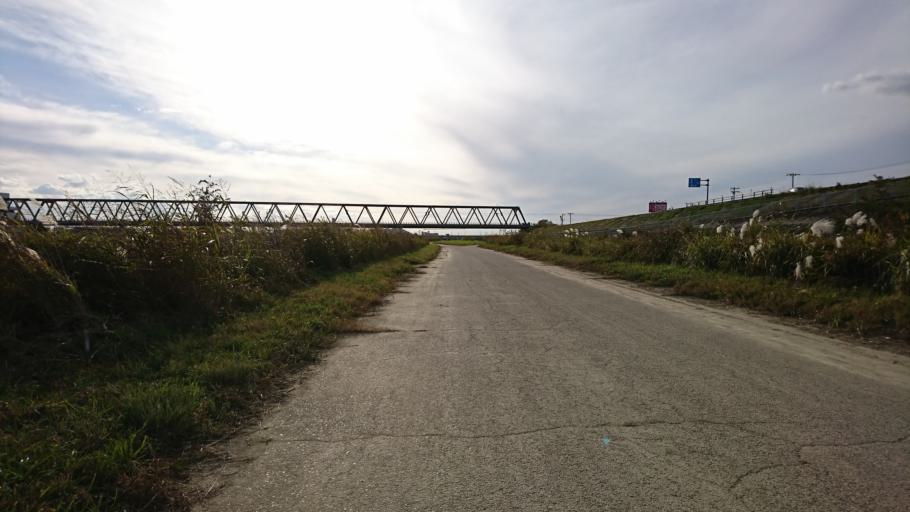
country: JP
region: Hyogo
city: Kakogawacho-honmachi
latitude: 34.7762
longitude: 134.8344
